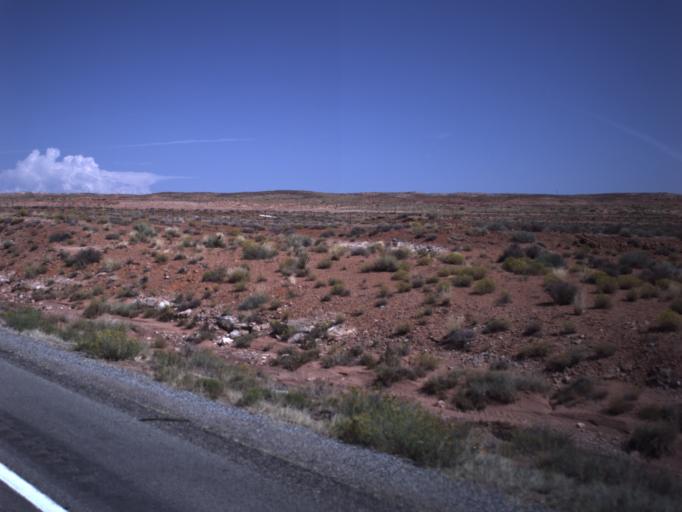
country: US
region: Utah
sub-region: San Juan County
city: Blanding
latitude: 36.9989
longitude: -109.6092
